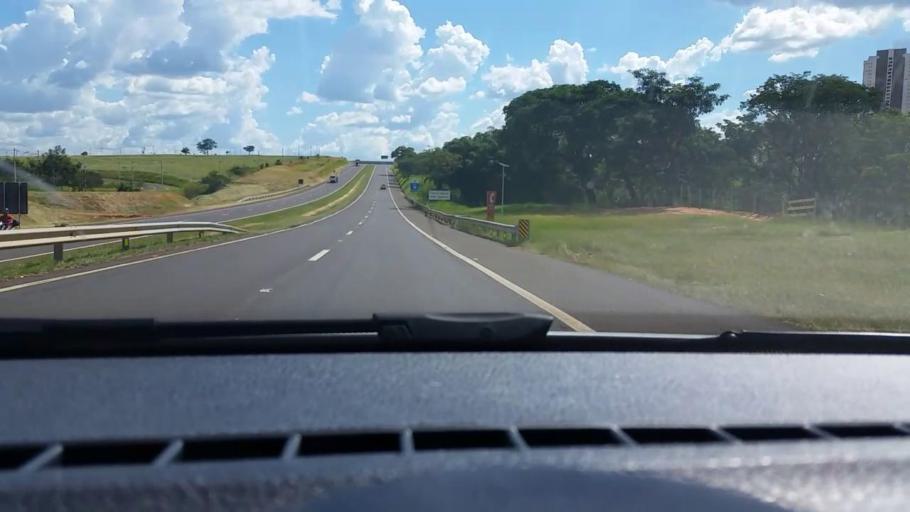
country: BR
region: Sao Paulo
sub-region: Bauru
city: Bauru
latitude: -22.3713
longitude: -49.0528
